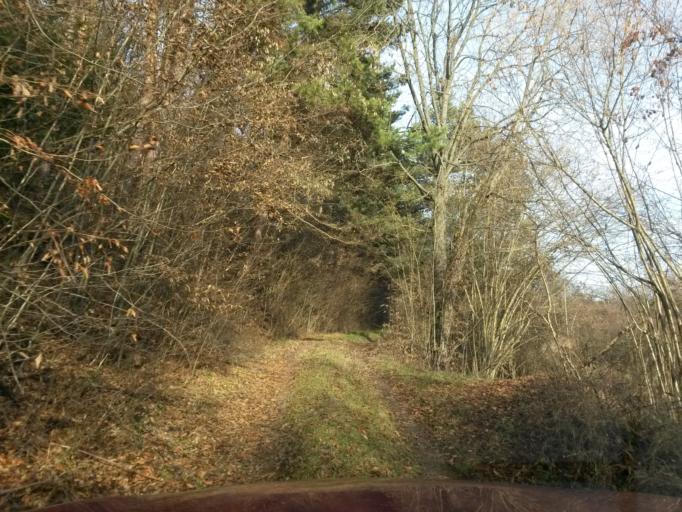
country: SK
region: Kosicky
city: Dobsina
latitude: 48.7266
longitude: 20.3858
